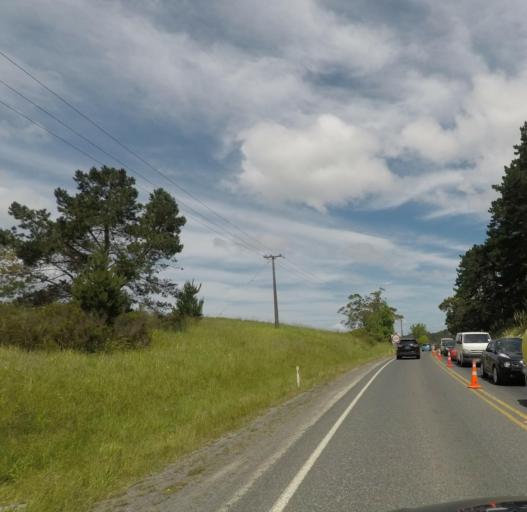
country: NZ
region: Auckland
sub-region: Auckland
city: Rothesay Bay
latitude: -36.6716
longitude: 174.6841
